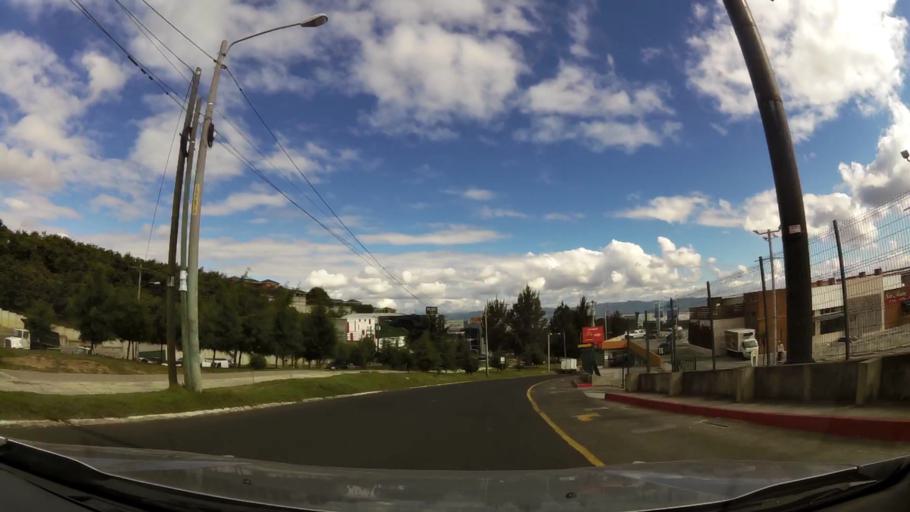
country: GT
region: Guatemala
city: Mixco
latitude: 14.6136
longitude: -90.6011
